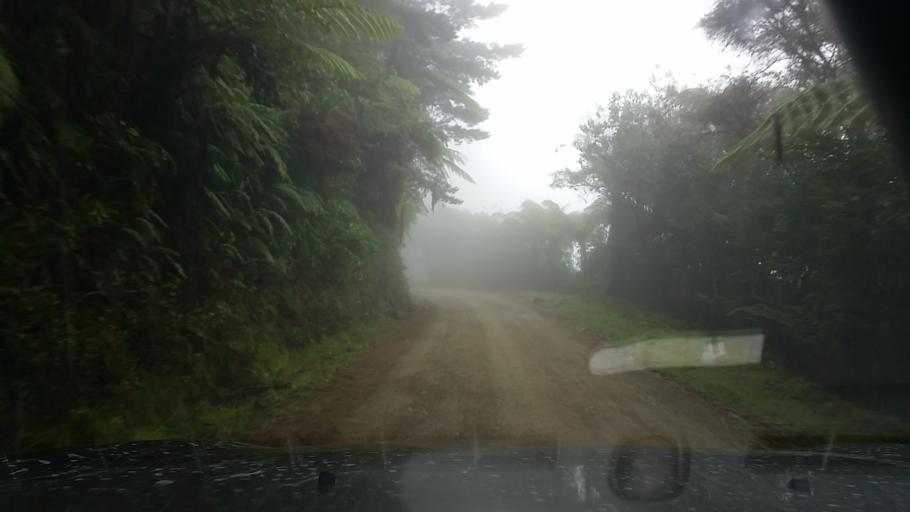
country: NZ
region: Marlborough
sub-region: Marlborough District
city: Picton
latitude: -41.1628
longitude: 173.9700
